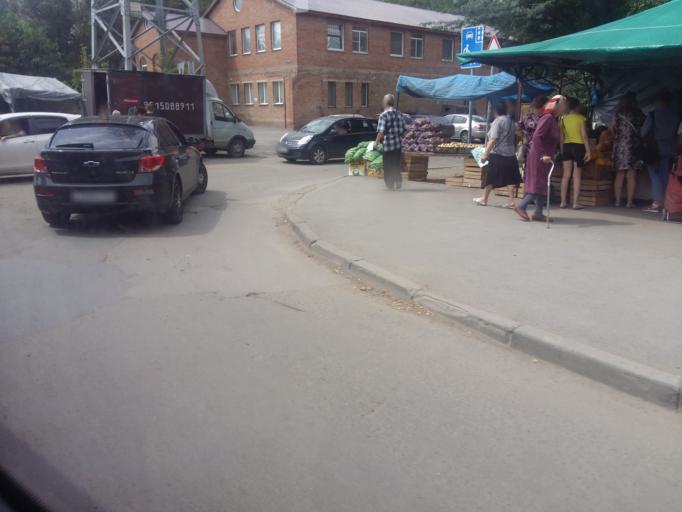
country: RU
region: Rostov
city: Imeni Chkalova
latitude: 47.2857
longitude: 39.7572
